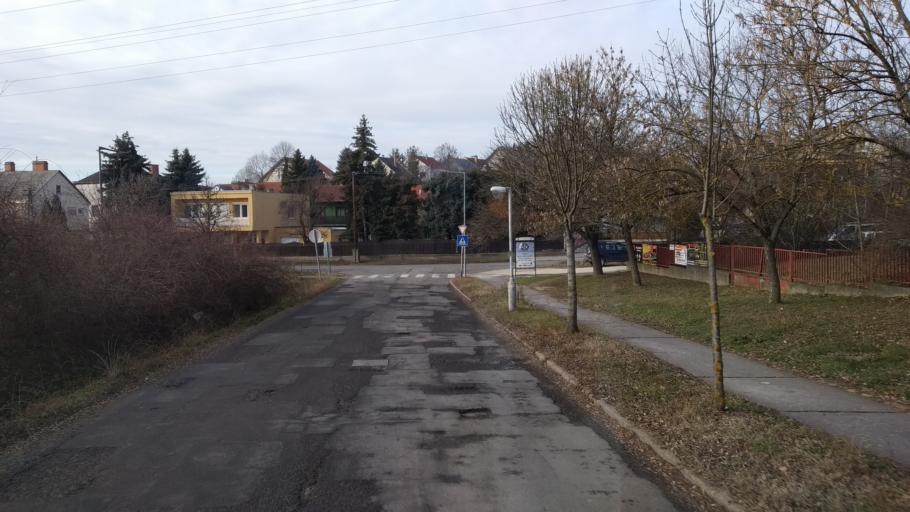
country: HU
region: Pest
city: Vac
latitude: 47.7837
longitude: 19.1444
